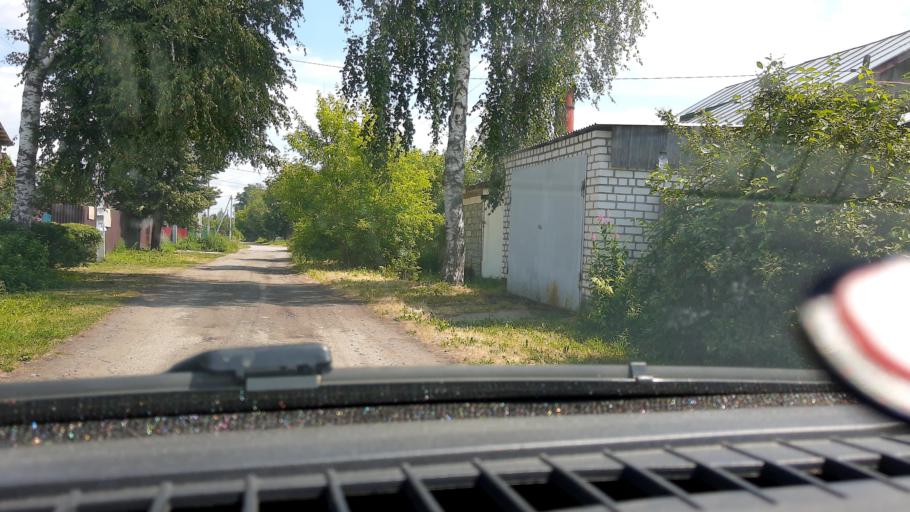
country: RU
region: Nizjnij Novgorod
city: Gorbatovka
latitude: 56.2718
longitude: 43.7530
